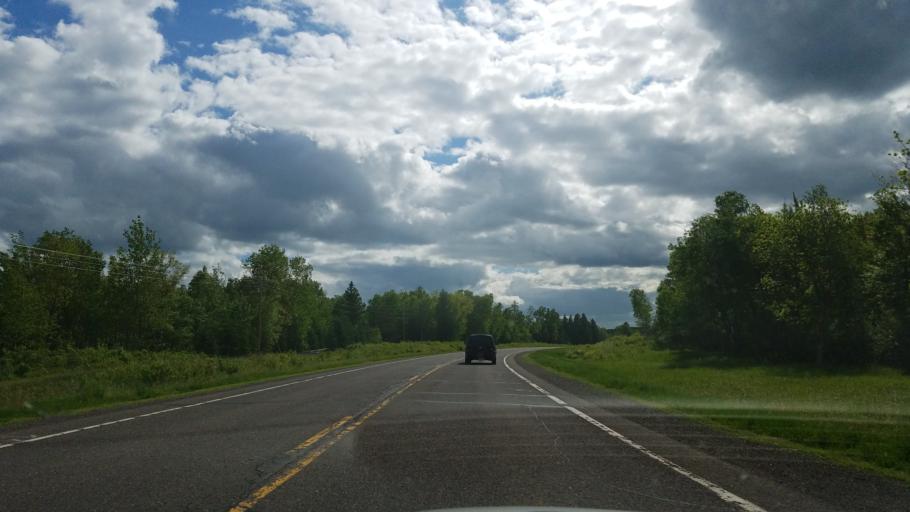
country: US
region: Wisconsin
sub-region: Burnett County
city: Siren
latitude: 46.1763
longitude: -92.2101
